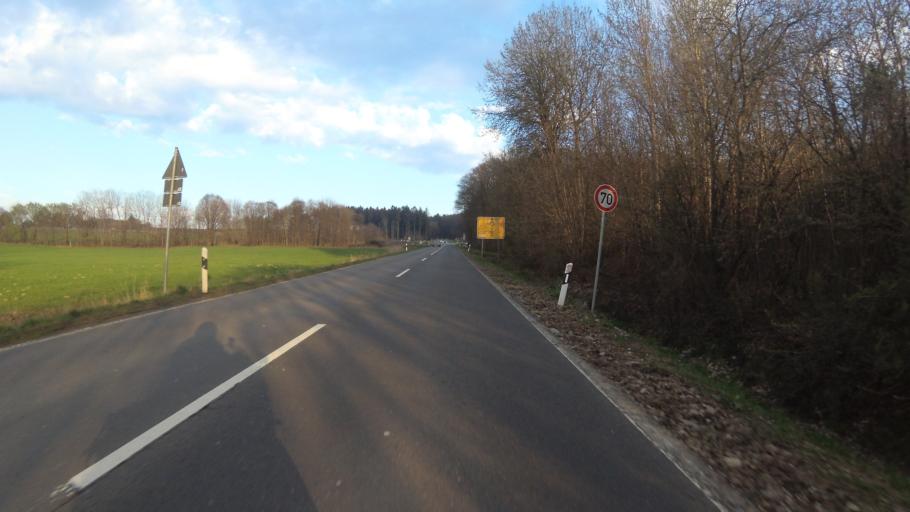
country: DE
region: Rheinland-Pfalz
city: Longkamp
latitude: 49.8751
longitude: 7.1128
